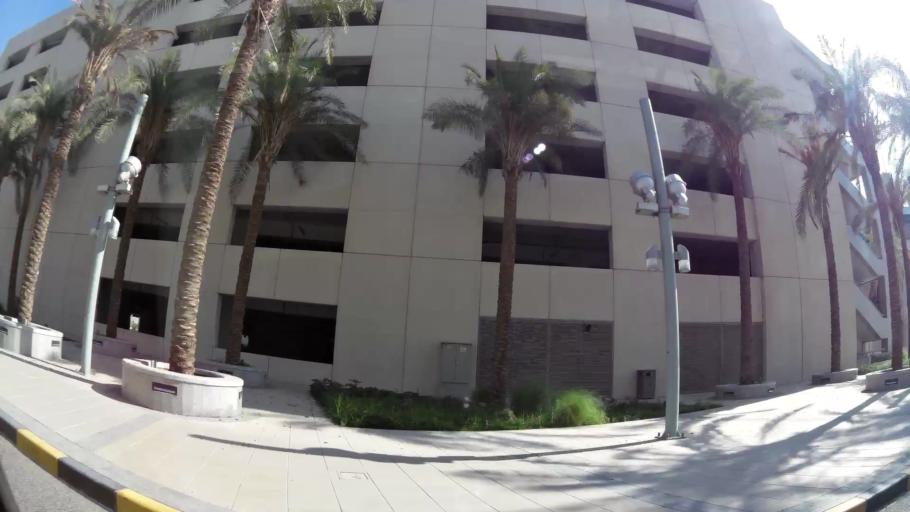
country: KW
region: Al Asimah
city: Kuwait City
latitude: 29.3638
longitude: 47.9822
